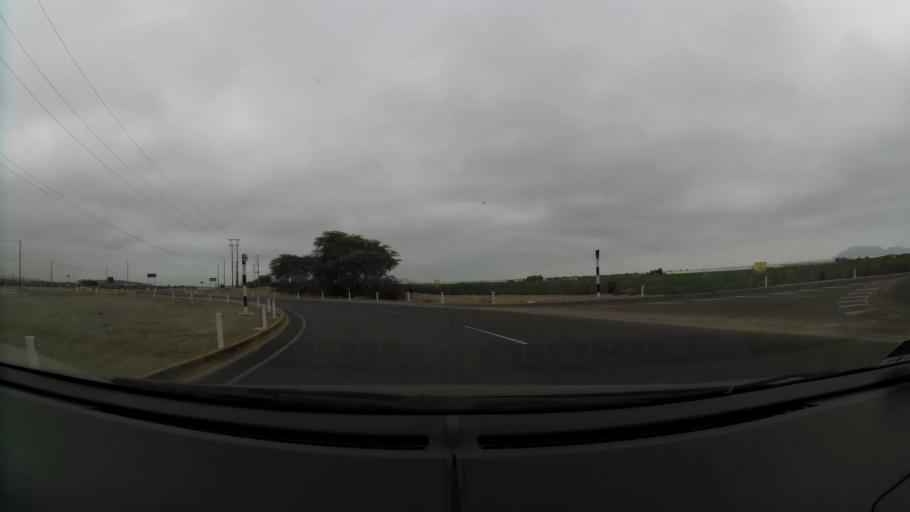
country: PE
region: La Libertad
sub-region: Viru
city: Viru
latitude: -8.3709
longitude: -78.8666
